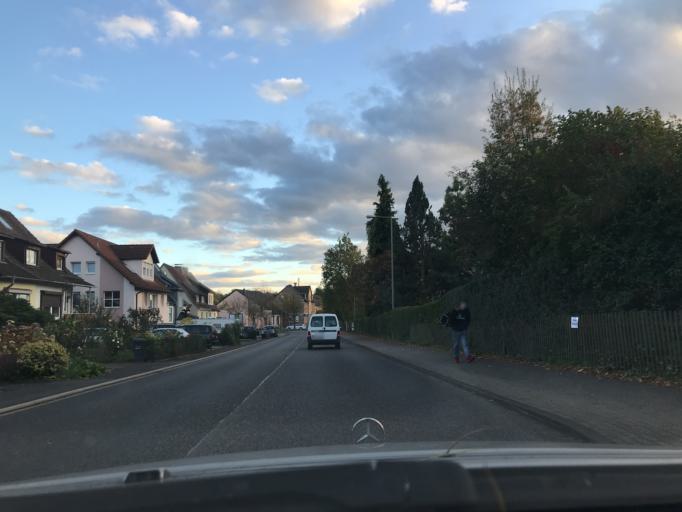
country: DE
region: Hesse
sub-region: Regierungsbezirk Kassel
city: Fuldabruck
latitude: 51.2810
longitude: 9.4533
